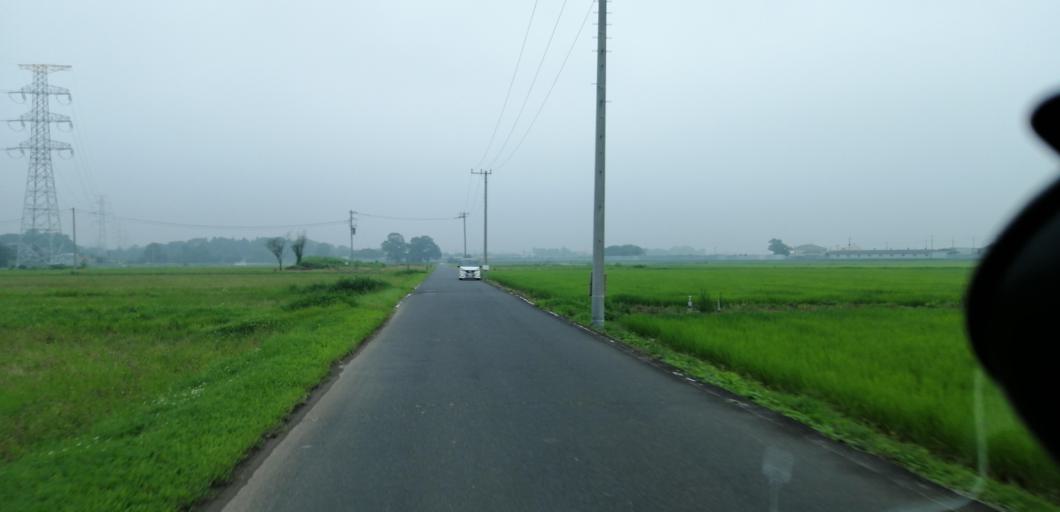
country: JP
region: Chiba
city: Noda
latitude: 35.9962
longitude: 139.8650
